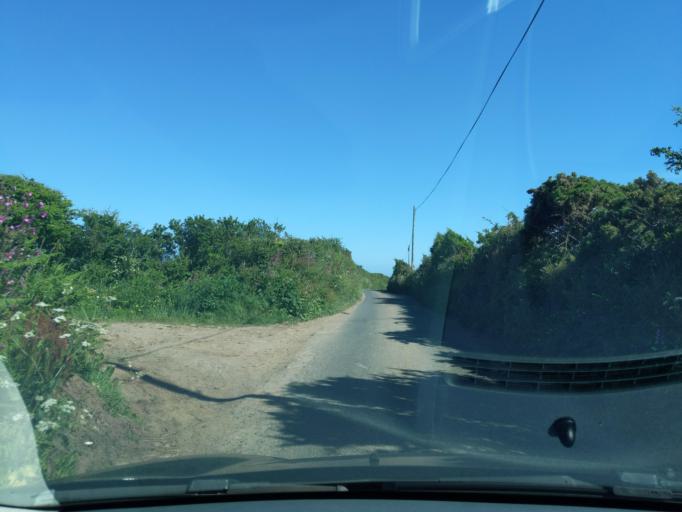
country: GB
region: England
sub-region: Cornwall
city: St. Buryan
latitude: 50.0638
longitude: -5.5998
